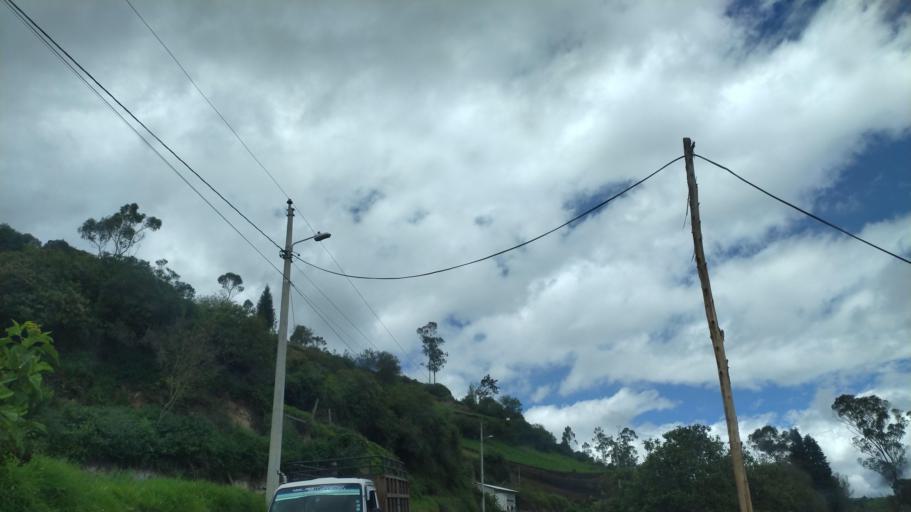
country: EC
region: Chimborazo
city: Riobamba
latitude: -1.6857
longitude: -78.5764
